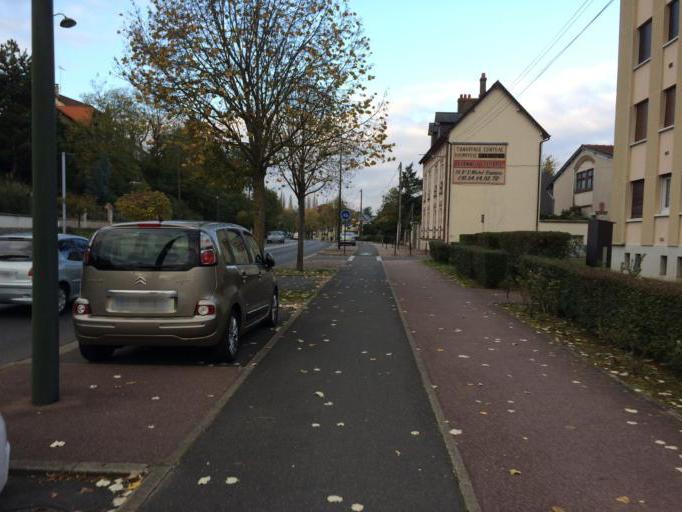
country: FR
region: Ile-de-France
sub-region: Departement de l'Essonne
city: Morigny-Champigny
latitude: 48.4454
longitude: 2.1708
